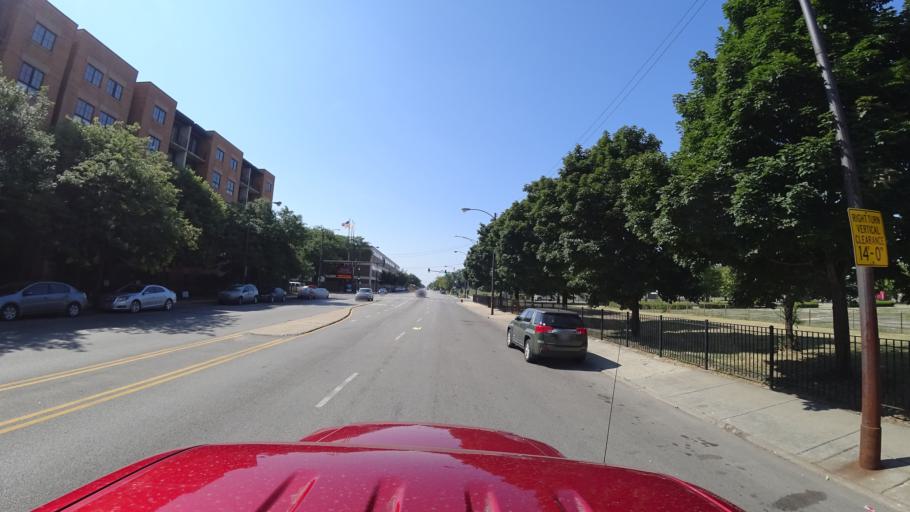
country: US
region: Illinois
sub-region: Cook County
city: Chicago
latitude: 41.8245
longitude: -87.6265
